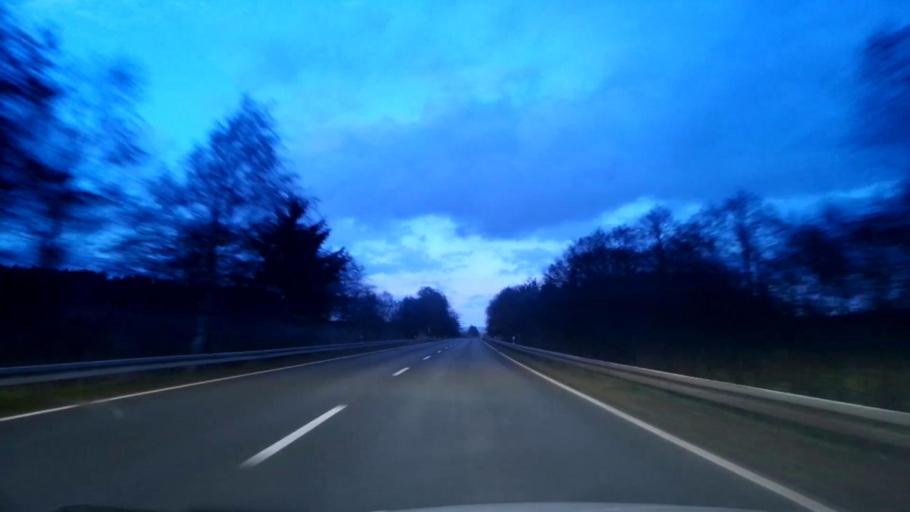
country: DE
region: Bavaria
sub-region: Upper Palatinate
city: Waldershof
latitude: 49.9595
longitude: 12.0935
